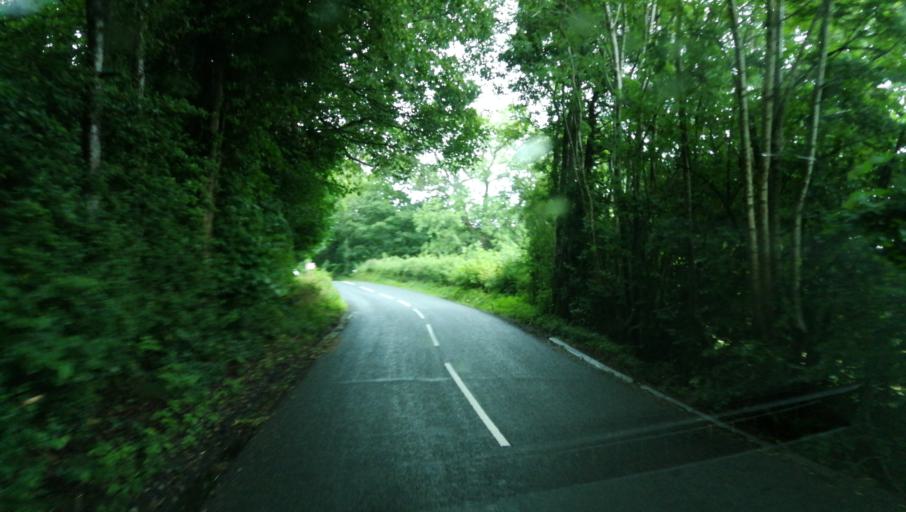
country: GB
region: England
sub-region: Cumbria
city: Penrith
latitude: 54.5913
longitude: -2.8594
